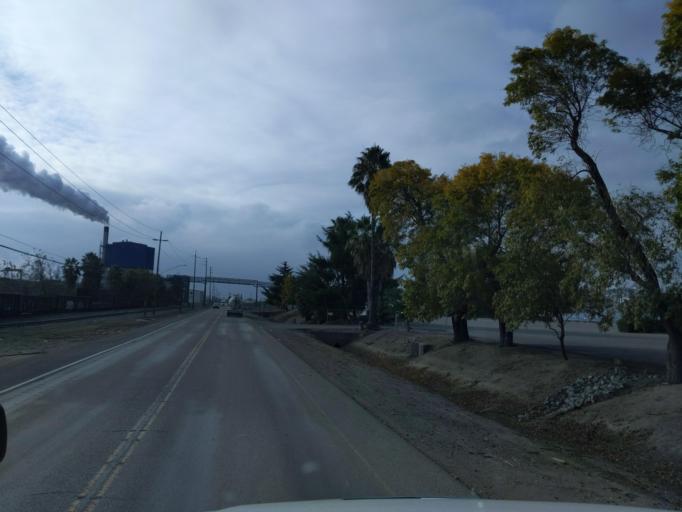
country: US
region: California
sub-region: San Joaquin County
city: Country Club
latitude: 37.9448
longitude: -121.3261
